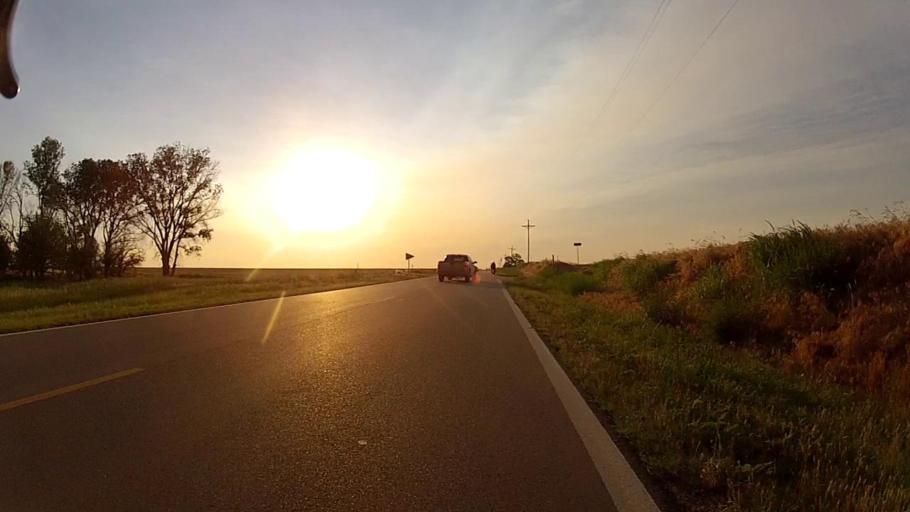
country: US
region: Kansas
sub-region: Harper County
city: Anthony
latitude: 37.1526
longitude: -97.9484
